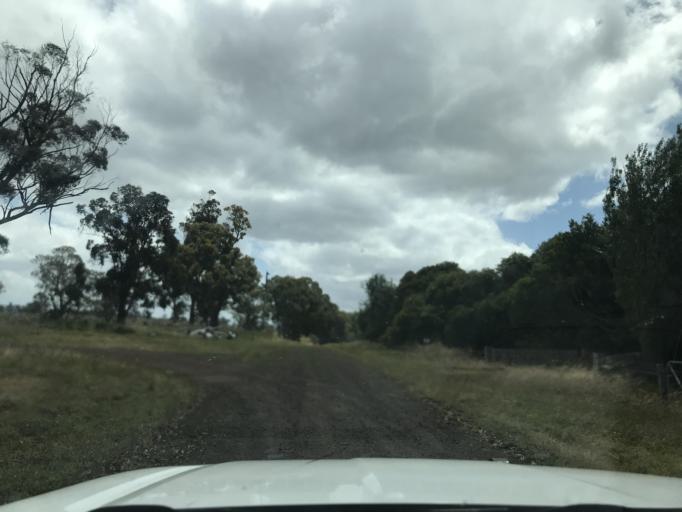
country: AU
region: South Australia
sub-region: Wattle Range
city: Penola
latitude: -37.2978
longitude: 141.4756
